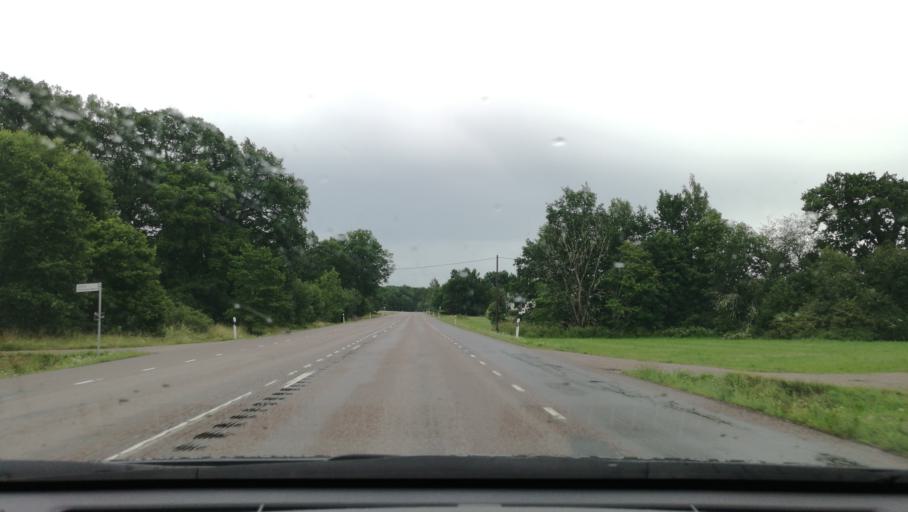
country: SE
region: Vaestmanland
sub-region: Kungsors Kommun
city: Kungsoer
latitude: 59.4420
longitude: 16.0470
